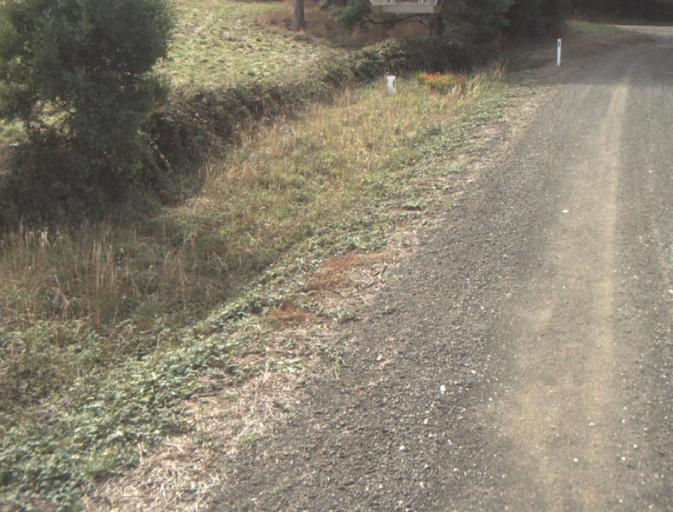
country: AU
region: Tasmania
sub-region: Launceston
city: Mayfield
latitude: -41.1946
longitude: 147.1951
